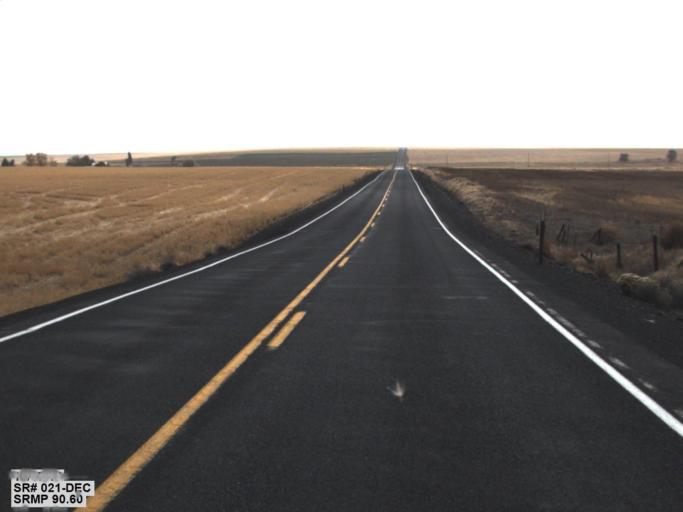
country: US
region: Washington
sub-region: Okanogan County
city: Coulee Dam
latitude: 47.7501
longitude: -118.7217
